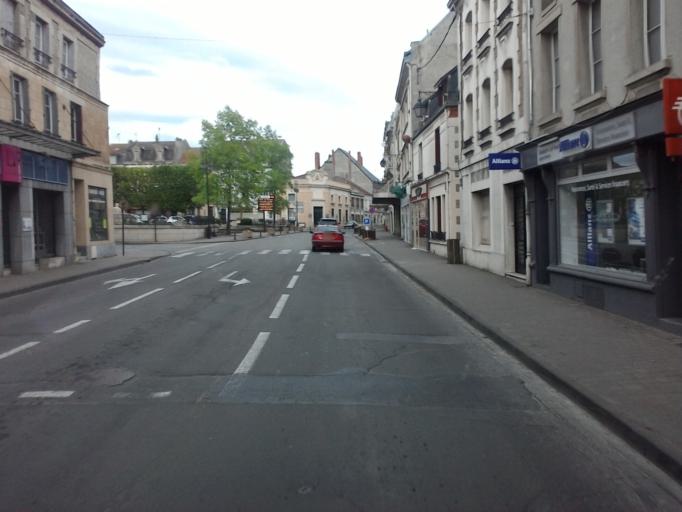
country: FR
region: Champagne-Ardenne
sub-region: Departement des Ardennes
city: Vouziers
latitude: 49.3976
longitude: 4.6996
